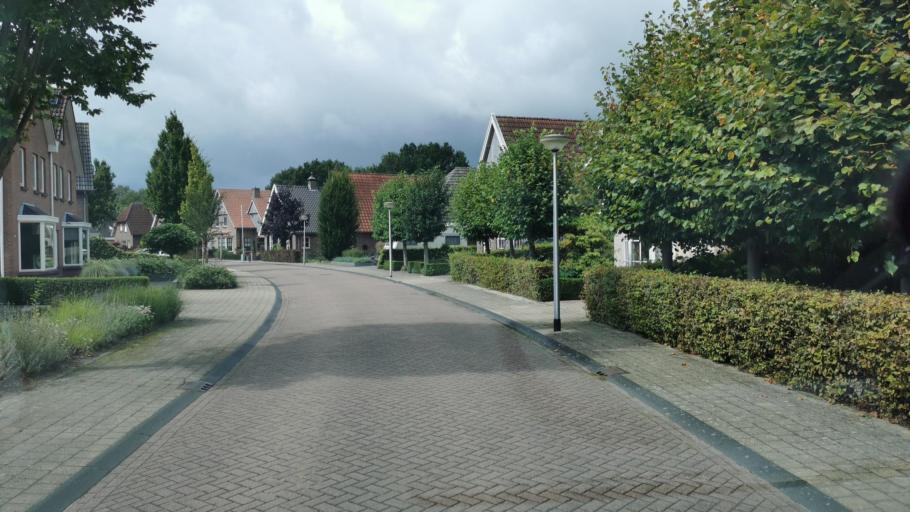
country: NL
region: Overijssel
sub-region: Gemeente Losser
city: Losser
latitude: 52.2737
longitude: 7.0018
